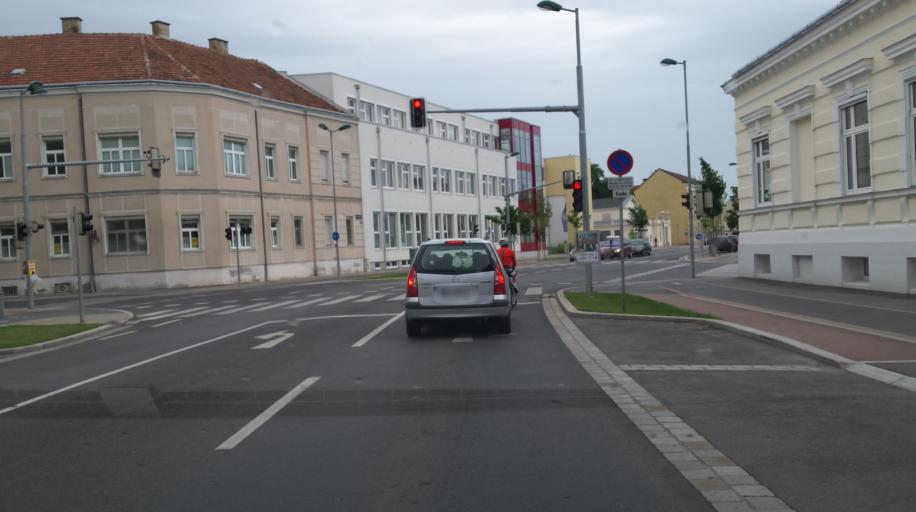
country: AT
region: Burgenland
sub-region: Politischer Bezirk Neusiedl am See
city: Bruckneudorf
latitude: 48.0254
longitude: 16.7757
